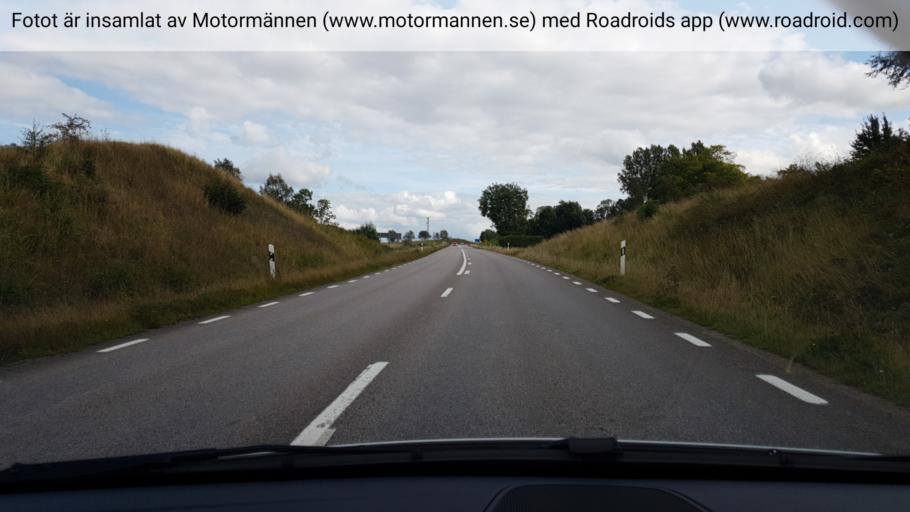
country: SE
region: Vaestra Goetaland
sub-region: Falkopings Kommun
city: Akarp
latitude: 58.1269
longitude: 13.6666
